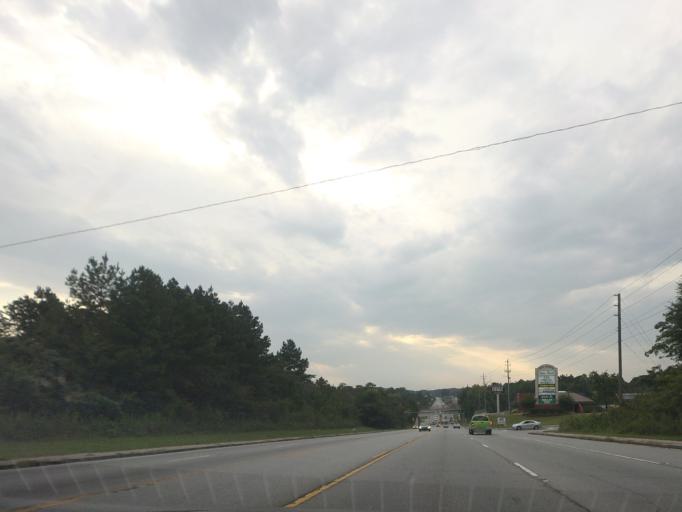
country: US
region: Georgia
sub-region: Bibb County
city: Macon
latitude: 32.8670
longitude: -83.6955
